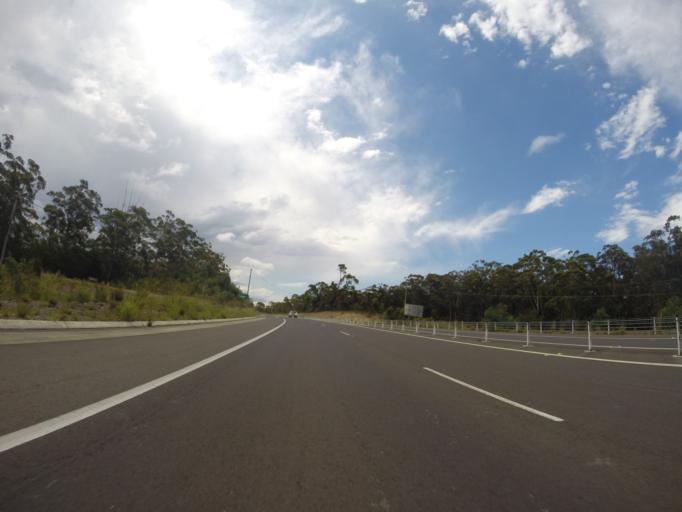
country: AU
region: New South Wales
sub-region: Shoalhaven Shire
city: Milton
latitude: -35.1987
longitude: 150.4415
